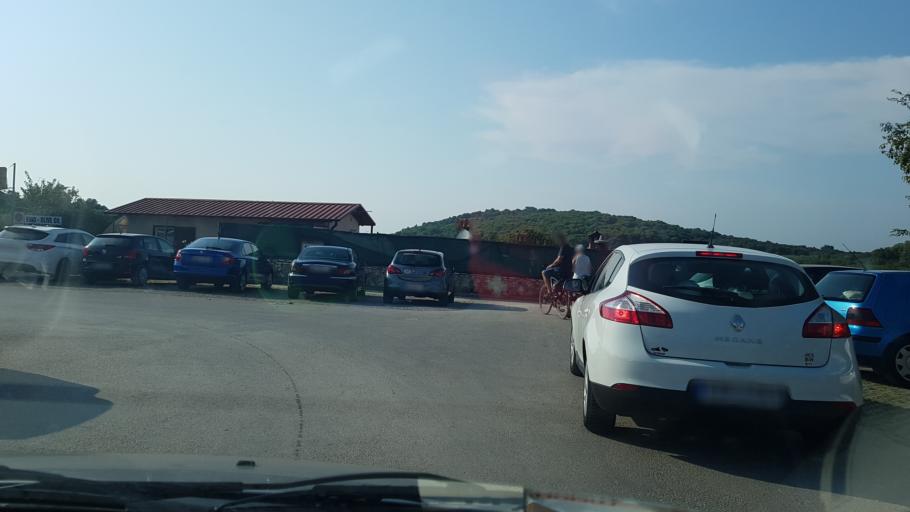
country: HR
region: Istarska
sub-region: Grad Rovinj
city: Rovinj
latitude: 45.1091
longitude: 13.6200
